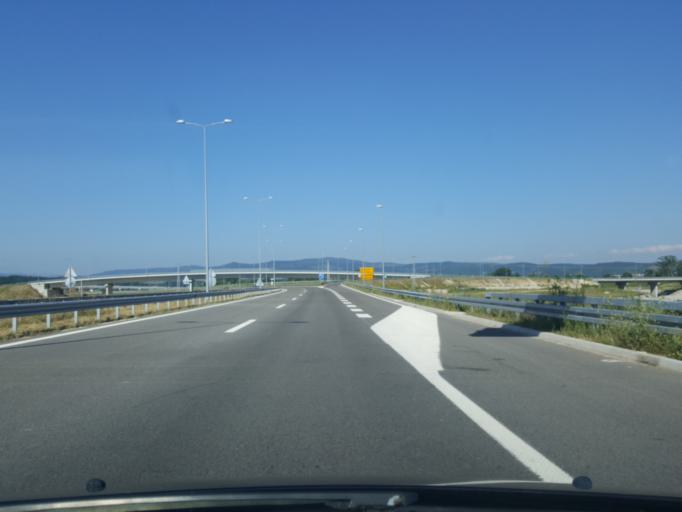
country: RS
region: Central Serbia
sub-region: Pcinjski Okrug
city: Bujanovac
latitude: 42.4514
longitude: 21.7836
